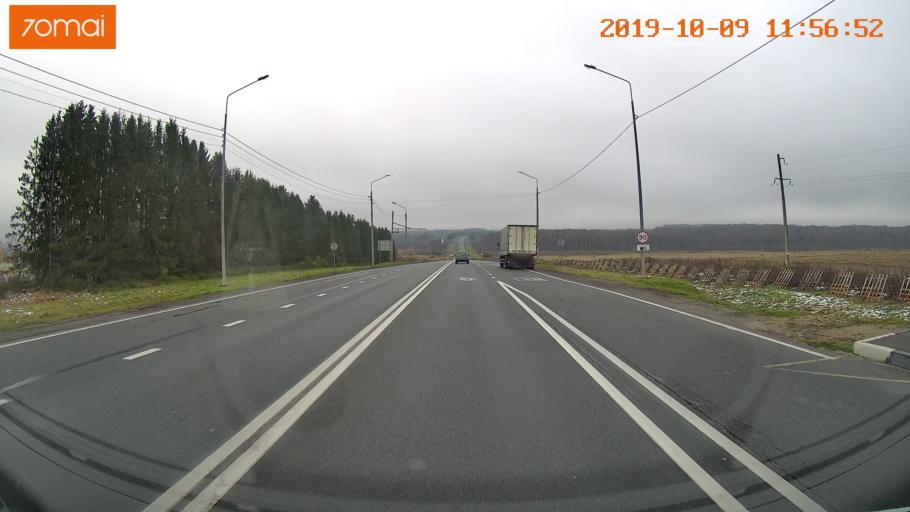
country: RU
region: Vologda
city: Gryazovets
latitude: 58.7392
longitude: 40.2896
